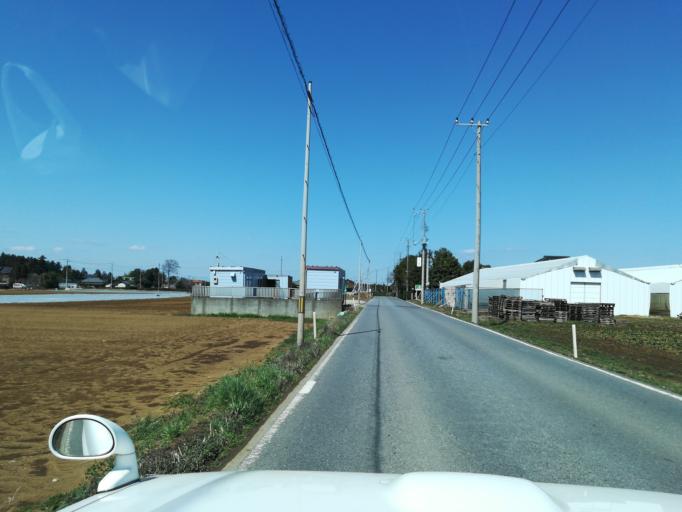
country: JP
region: Ibaraki
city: Ami
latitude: 35.9974
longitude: 140.1783
